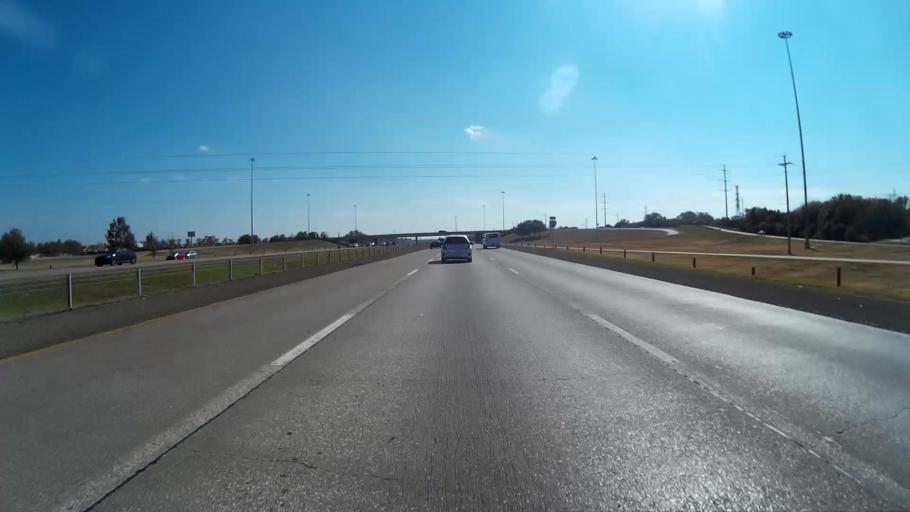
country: US
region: Texas
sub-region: Dallas County
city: Hutchins
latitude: 32.7040
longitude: -96.7541
